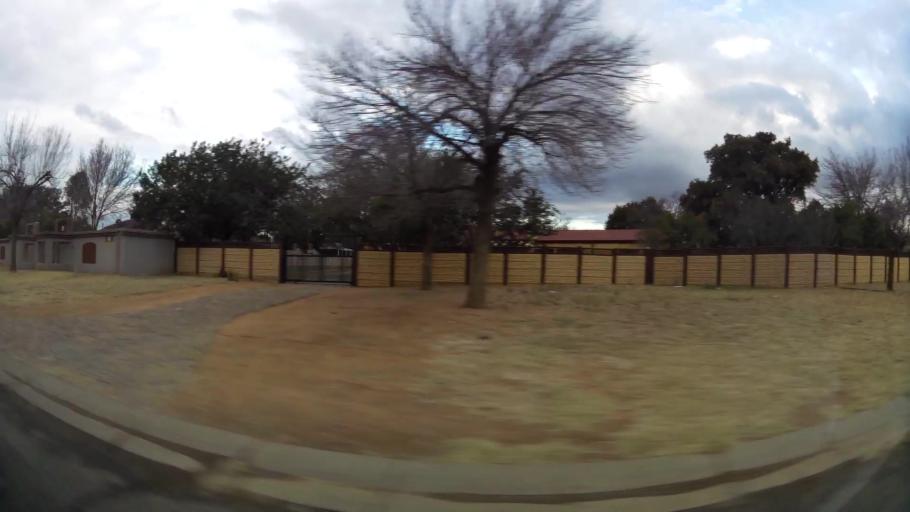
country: ZA
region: Orange Free State
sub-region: Lejweleputswa District Municipality
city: Welkom
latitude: -27.9542
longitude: 26.7393
